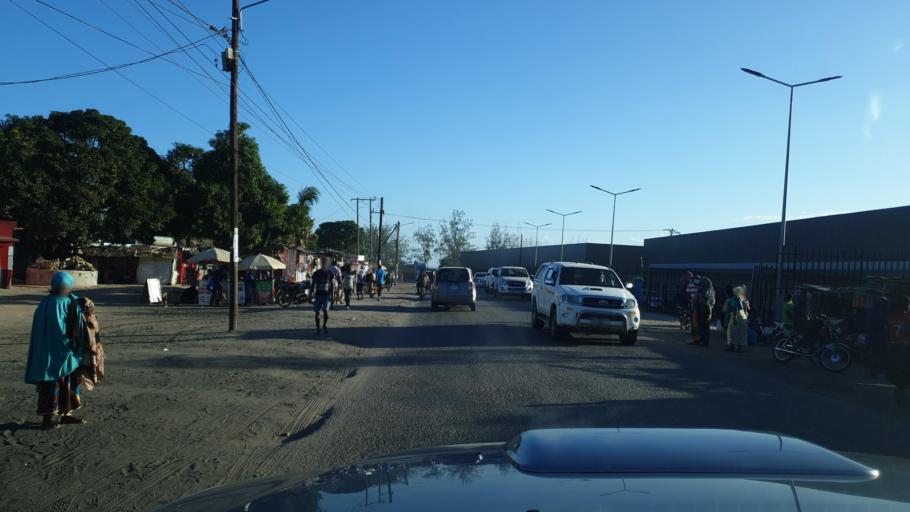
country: MZ
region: Nampula
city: Nacala
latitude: -14.5728
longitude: 40.6831
